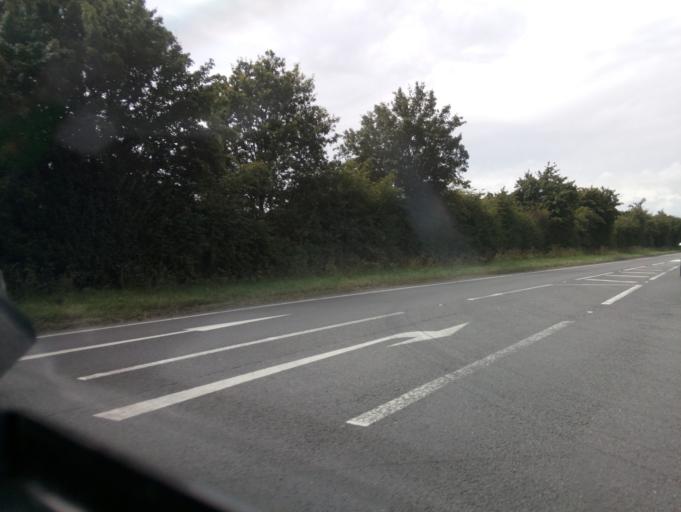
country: GB
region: England
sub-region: Somerset
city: Yeovil
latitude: 50.8733
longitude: -2.5976
